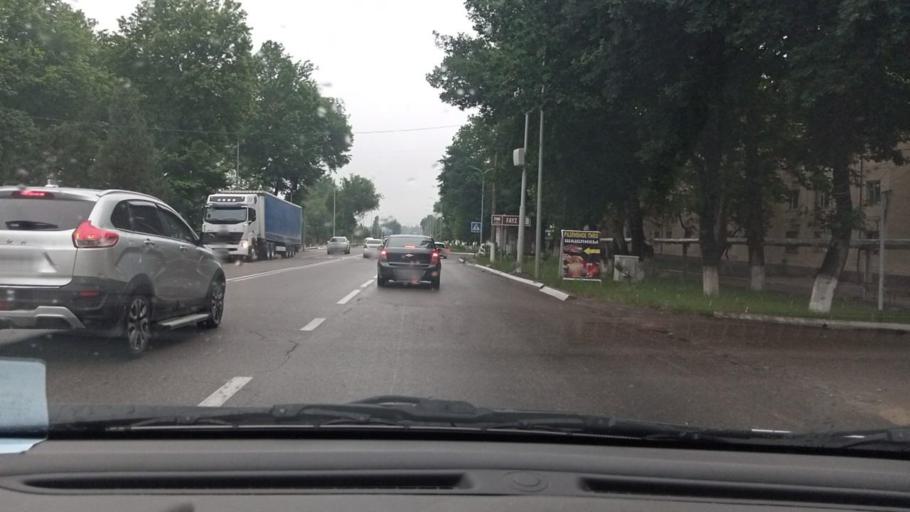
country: UZ
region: Toshkent
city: Angren
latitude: 40.9952
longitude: 70.0591
